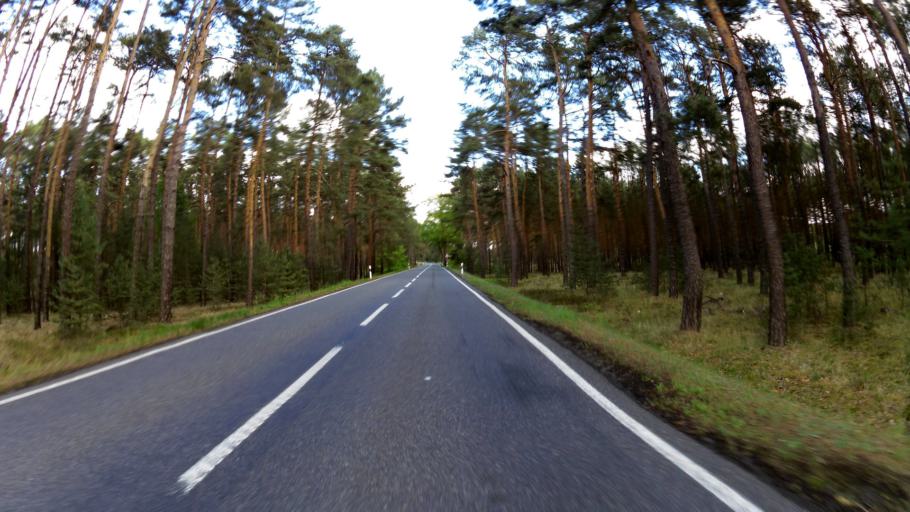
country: DE
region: Brandenburg
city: Wendisch Rietz
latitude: 52.1326
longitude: 13.9604
